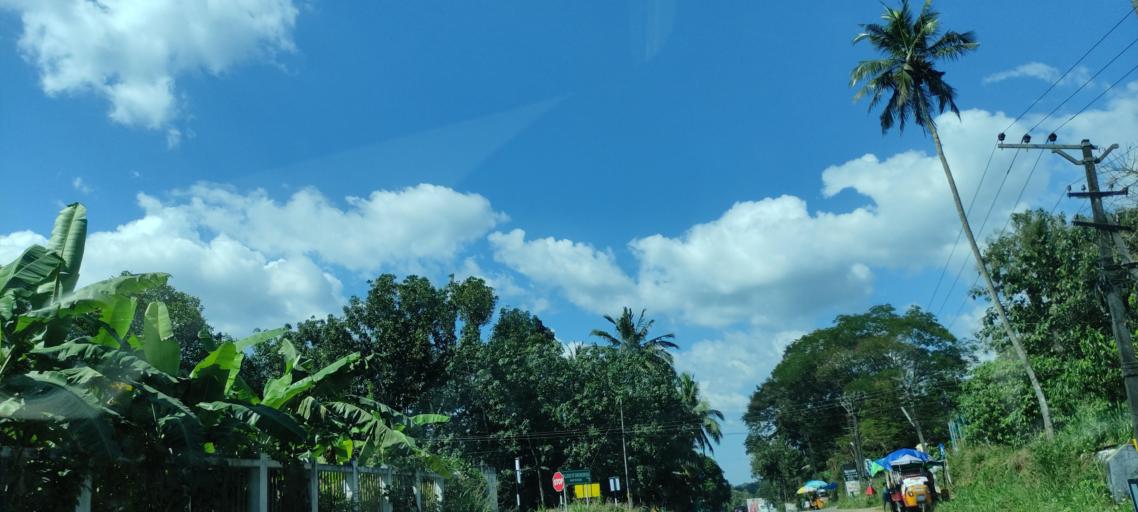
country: IN
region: Kerala
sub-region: Pattanamtitta
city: Adur
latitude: 9.1424
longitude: 76.7337
